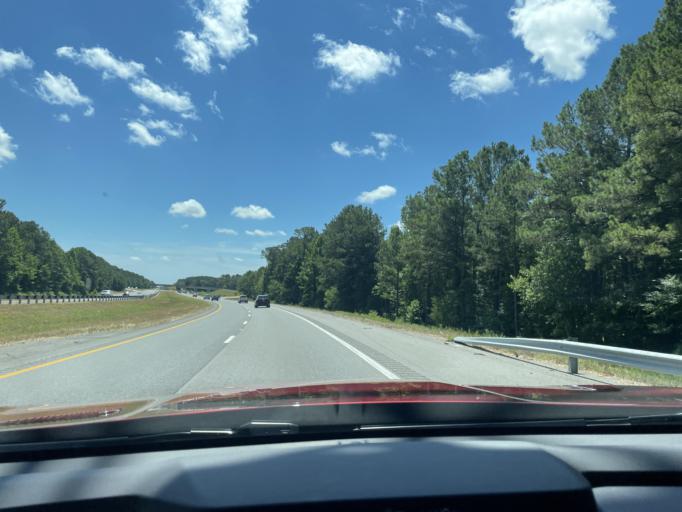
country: US
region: Arkansas
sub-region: Jefferson County
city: White Hall
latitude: 34.2474
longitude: -92.0997
